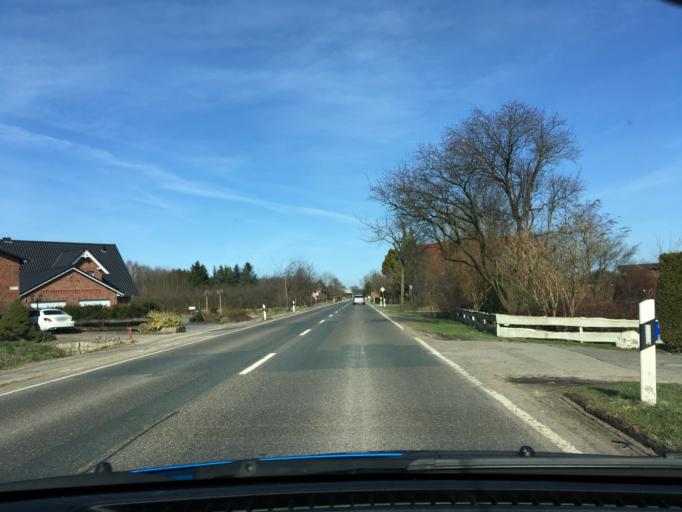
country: DE
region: Lower Saxony
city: Drage
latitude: 53.4238
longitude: 10.3015
